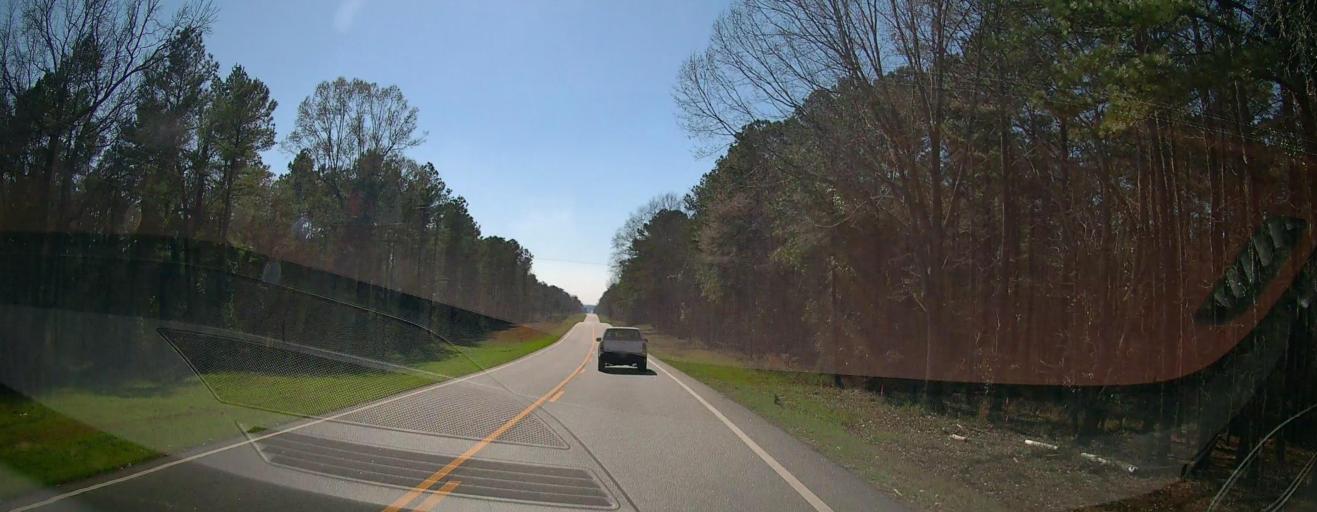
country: US
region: Georgia
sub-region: Dooly County
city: Unadilla
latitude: 32.3372
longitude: -83.8536
